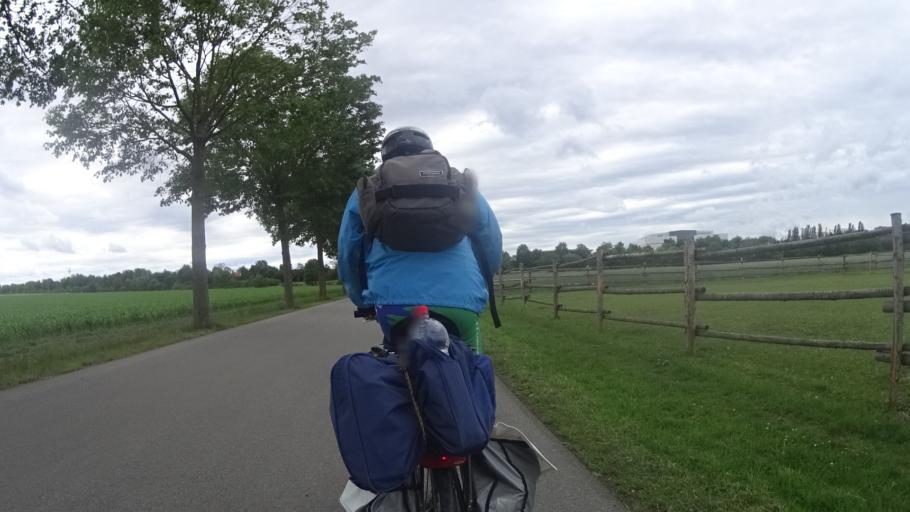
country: DE
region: Bavaria
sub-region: Upper Bavaria
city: Unterschleissheim
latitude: 48.2870
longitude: 11.5918
